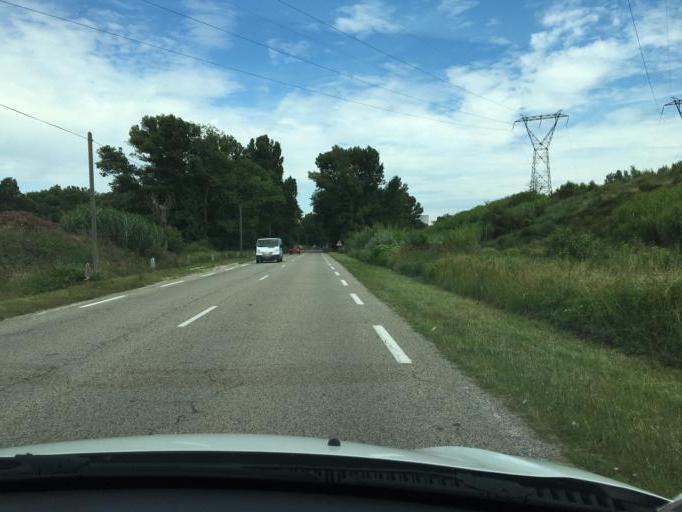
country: FR
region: Provence-Alpes-Cote d'Azur
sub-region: Departement du Vaucluse
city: Bollene
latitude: 44.3062
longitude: 4.7374
